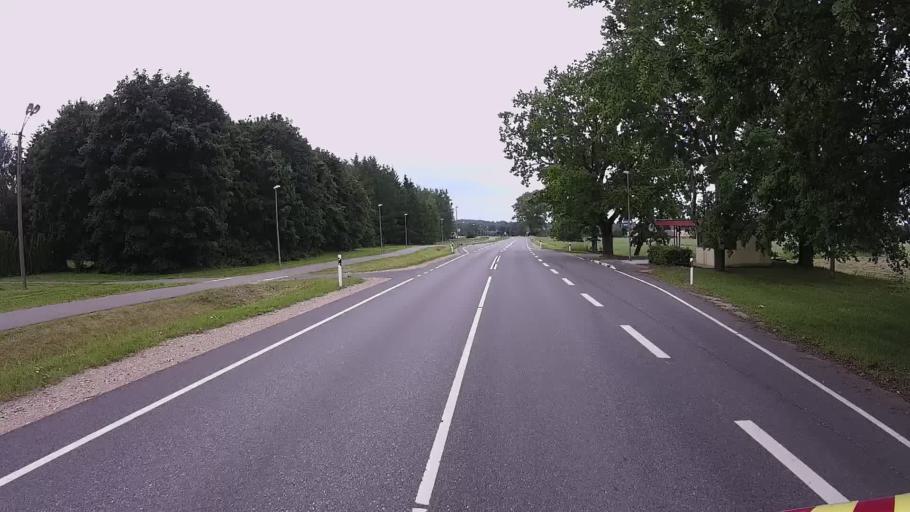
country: EE
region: Viljandimaa
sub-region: Karksi vald
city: Karksi-Nuia
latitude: 58.1193
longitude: 25.5817
